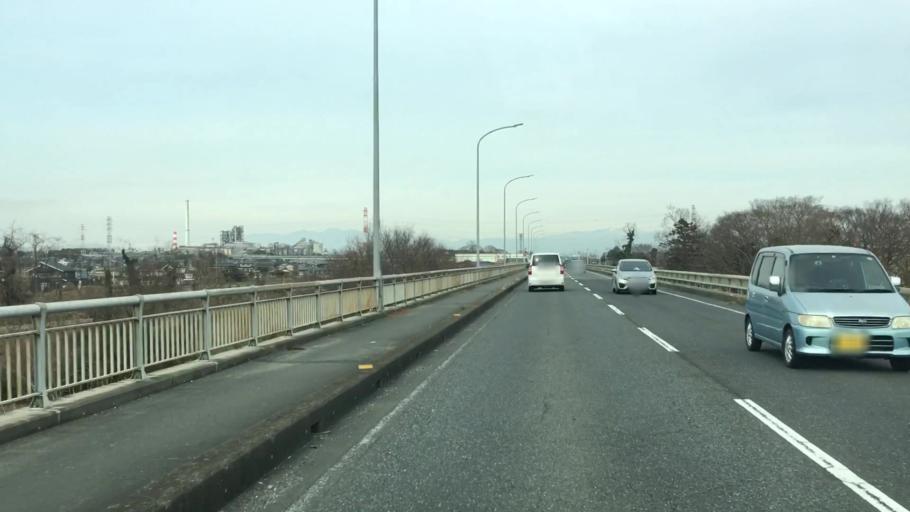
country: JP
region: Saitama
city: Kumagaya
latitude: 36.1420
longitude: 139.3230
